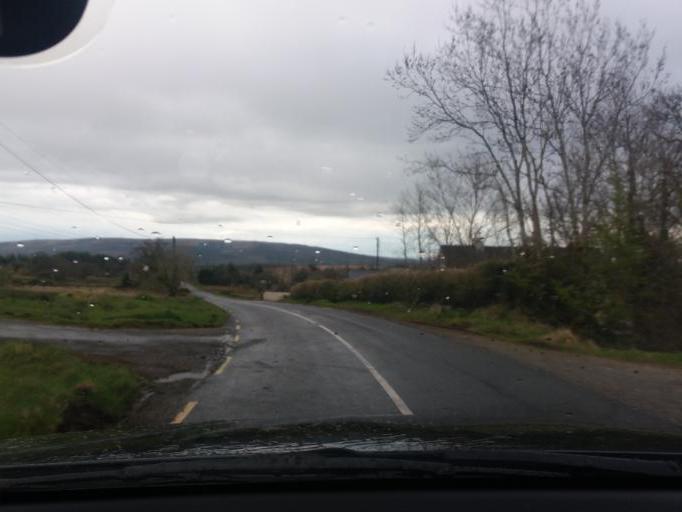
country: IE
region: Ulster
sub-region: An Cabhan
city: Ballyconnell
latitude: 54.1571
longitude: -7.7760
